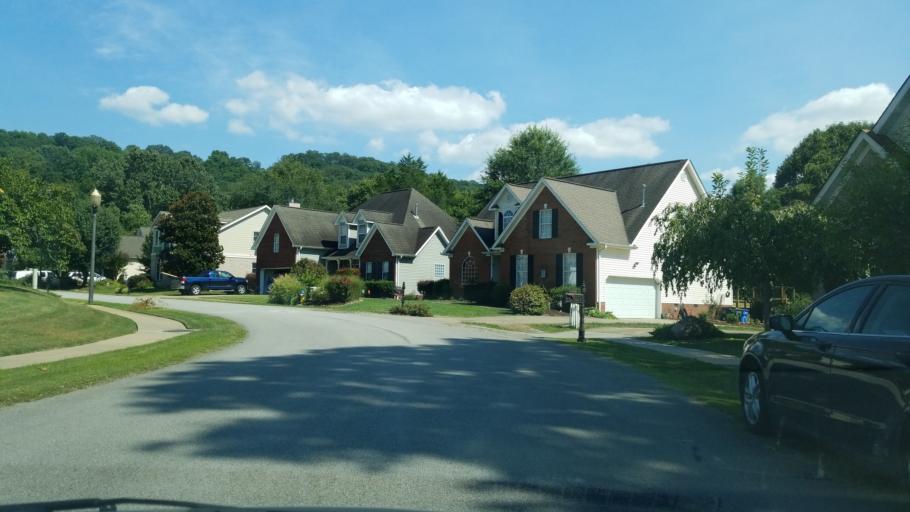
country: US
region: Tennessee
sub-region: Hamilton County
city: Middle Valley
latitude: 35.1357
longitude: -85.2132
